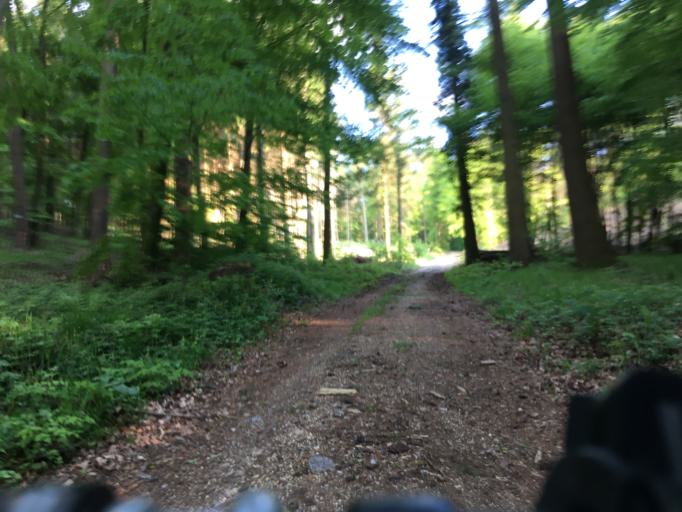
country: CH
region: Schaffhausen
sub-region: Bezirk Stein
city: Ramsen
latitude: 47.7047
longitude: 8.7912
